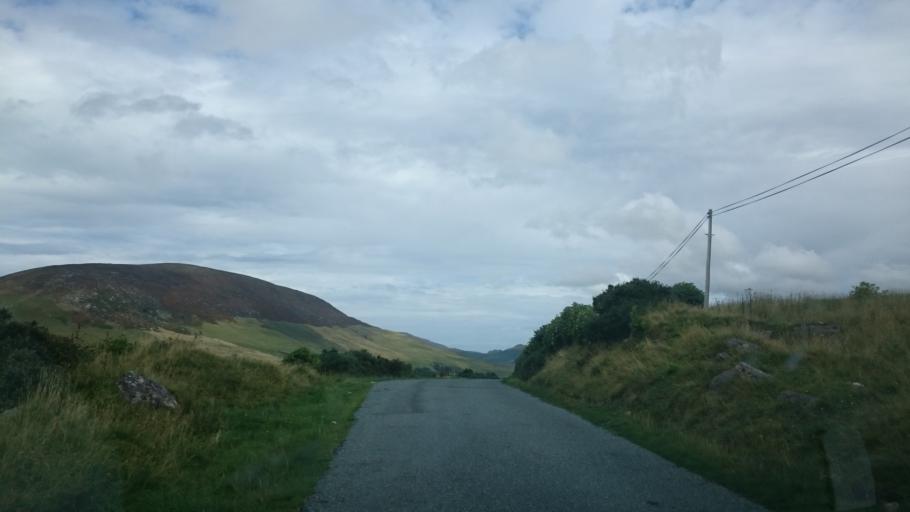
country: IE
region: Connaught
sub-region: Maigh Eo
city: Westport
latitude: 53.9538
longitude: -9.5692
